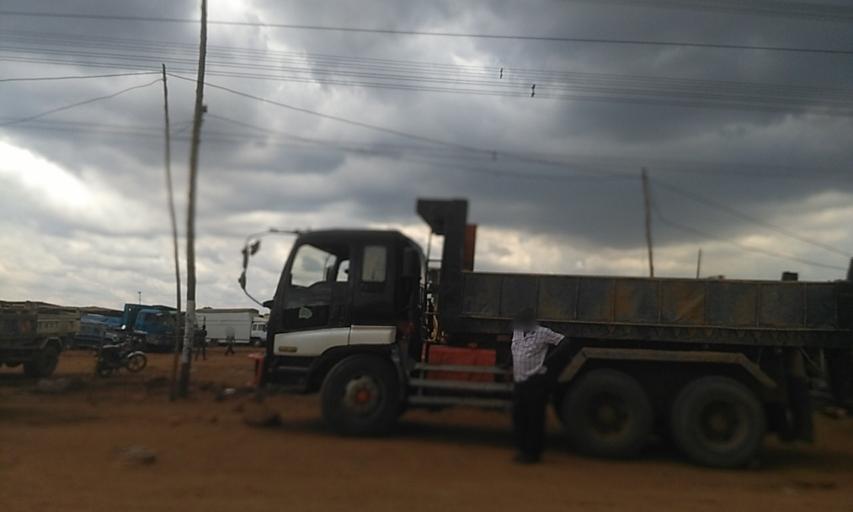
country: UG
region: Central Region
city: Kampala Central Division
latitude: 0.3159
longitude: 32.5121
